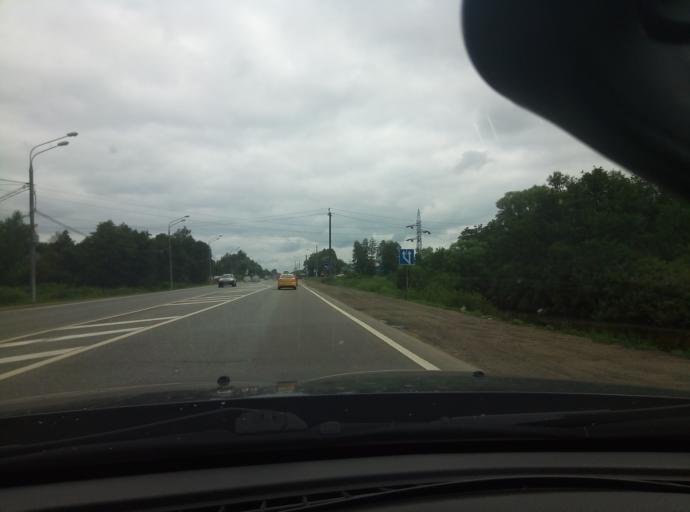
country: RU
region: Kaluga
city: Obninsk
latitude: 55.0869
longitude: 36.6330
